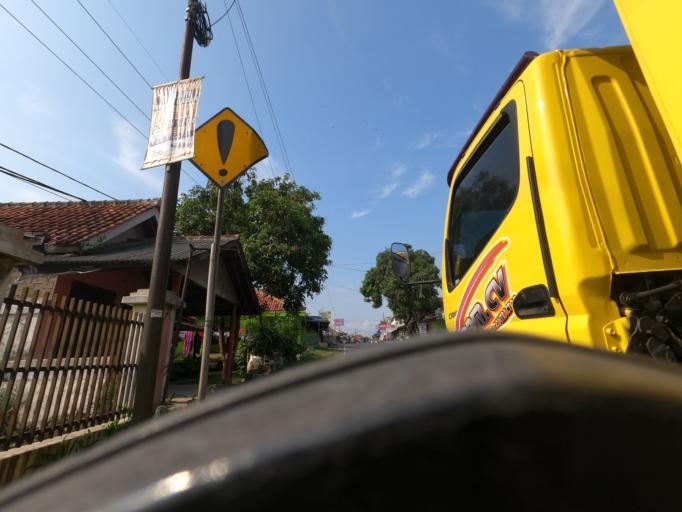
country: ID
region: West Java
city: Lembang
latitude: -6.6482
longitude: 107.7215
